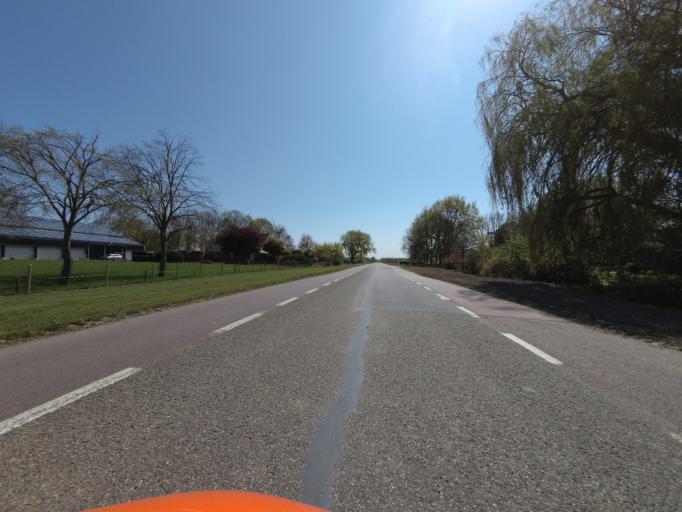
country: NL
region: Flevoland
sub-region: Gemeente Lelystad
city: Lelystad
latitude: 52.4007
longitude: 5.4264
